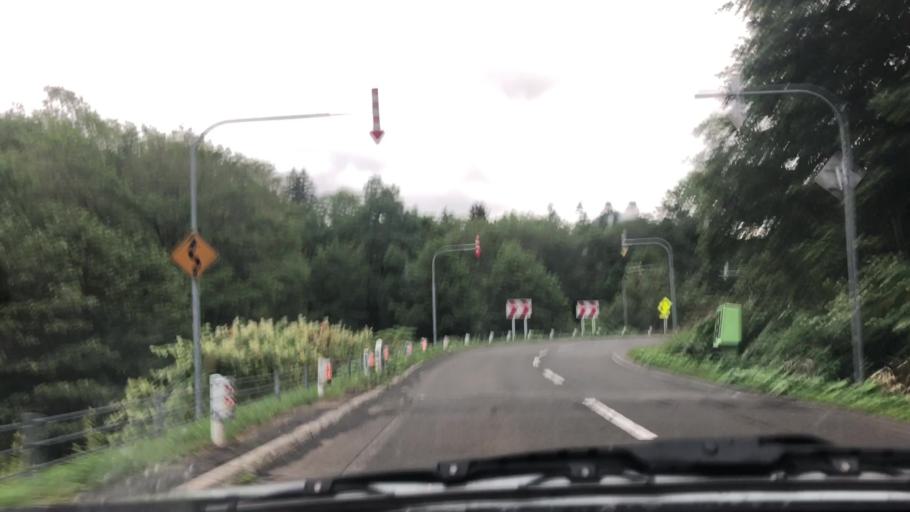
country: JP
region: Hokkaido
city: Shimo-furano
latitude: 42.9298
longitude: 142.3743
